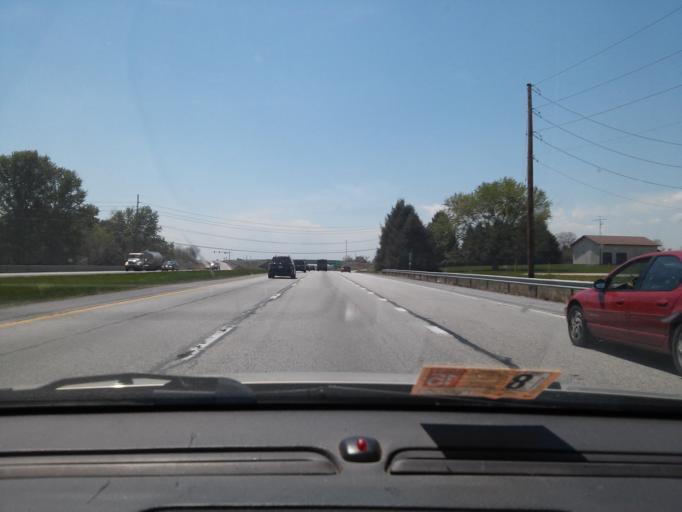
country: US
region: Pennsylvania
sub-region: Franklin County
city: Guilford
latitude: 39.9443
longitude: -77.6184
